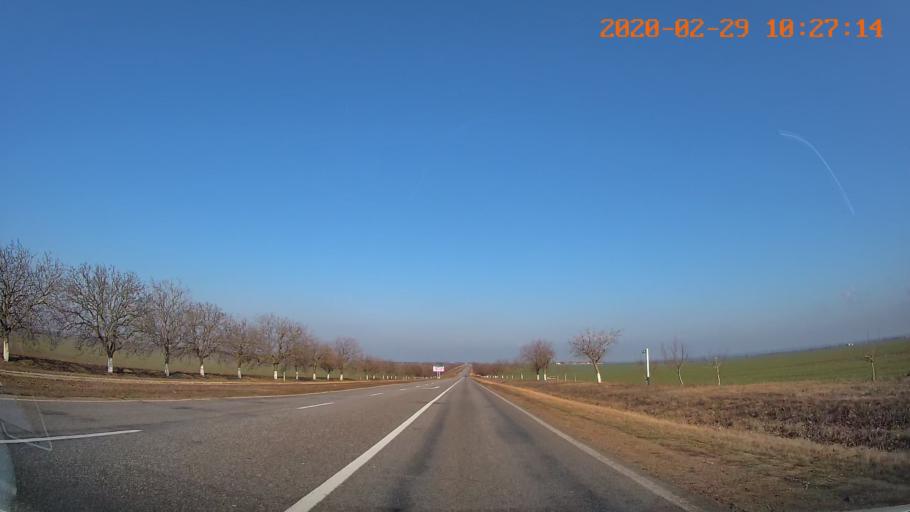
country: MD
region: Telenesti
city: Tiraspolul Nou
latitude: 46.8930
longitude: 29.5991
